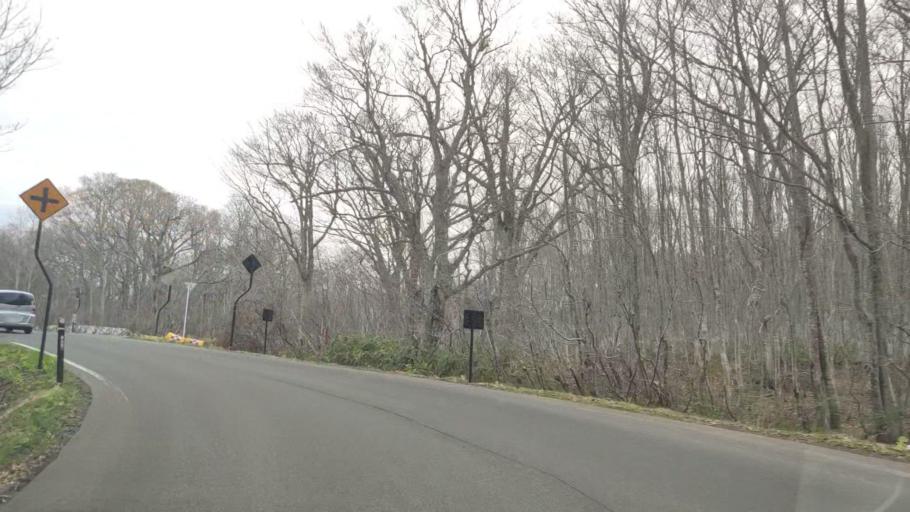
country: JP
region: Aomori
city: Aomori Shi
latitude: 40.6642
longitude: 140.9577
